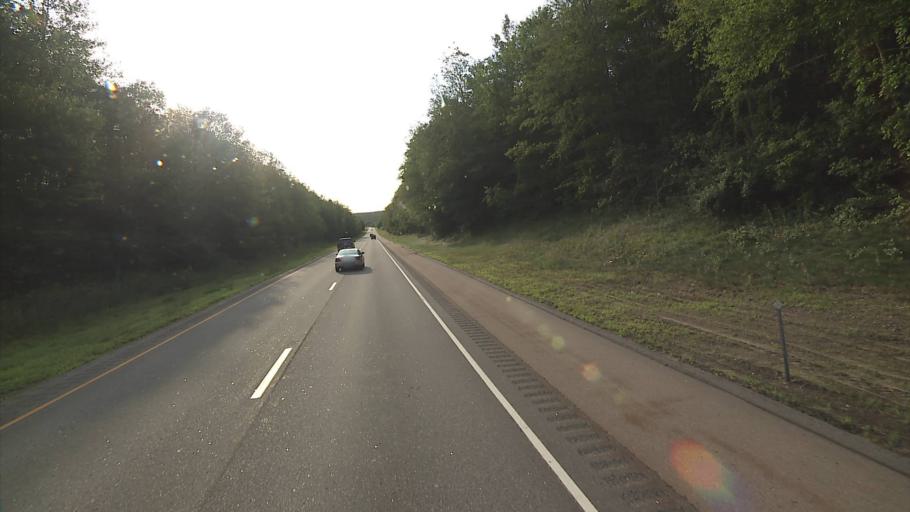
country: US
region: Connecticut
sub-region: New London County
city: Colchester
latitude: 41.5668
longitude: -72.2599
